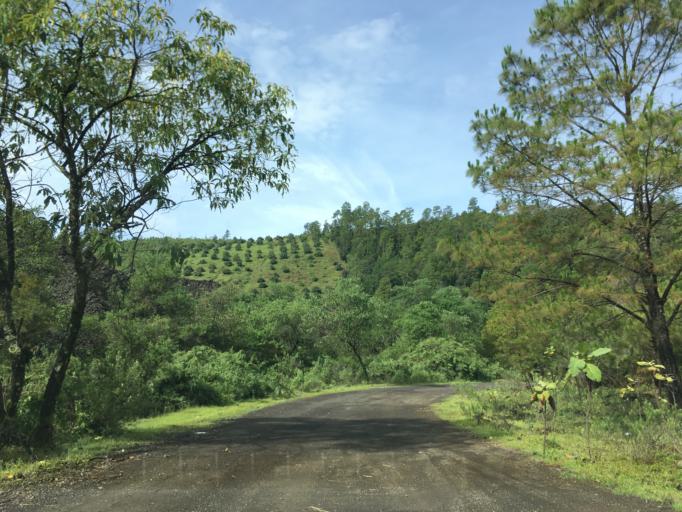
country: MX
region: Michoacan
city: Angahuan
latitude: 19.5264
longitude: -102.2364
